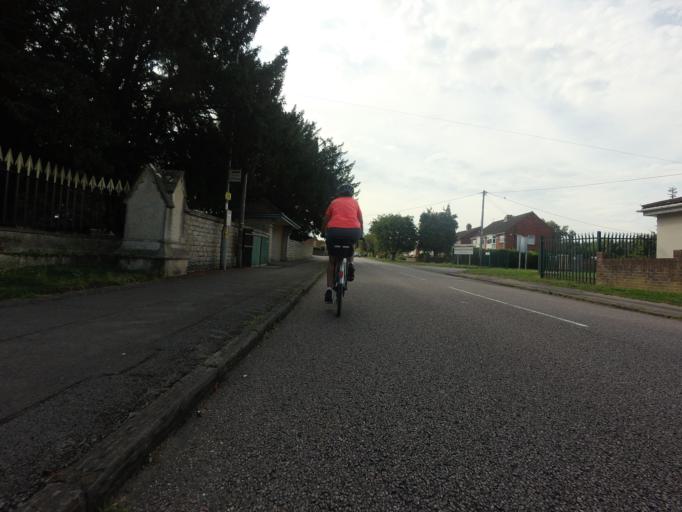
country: GB
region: England
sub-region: Wiltshire
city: Trowbridge
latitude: 51.3304
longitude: -2.2011
